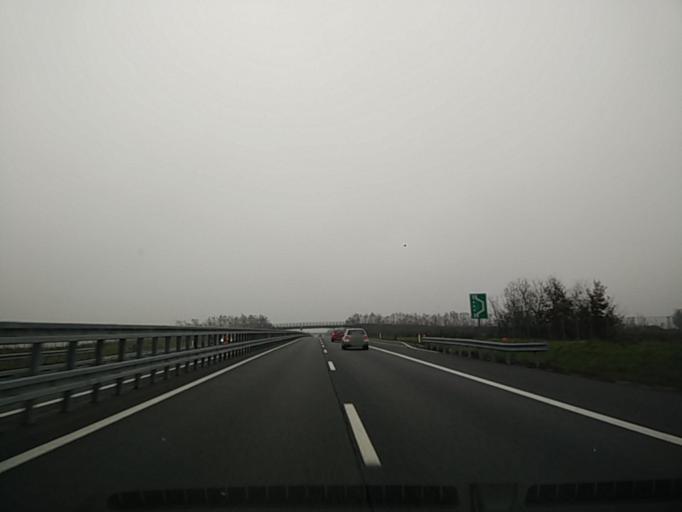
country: IT
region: Piedmont
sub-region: Provincia di Alessandria
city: Felizzano
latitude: 44.9171
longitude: 8.4461
